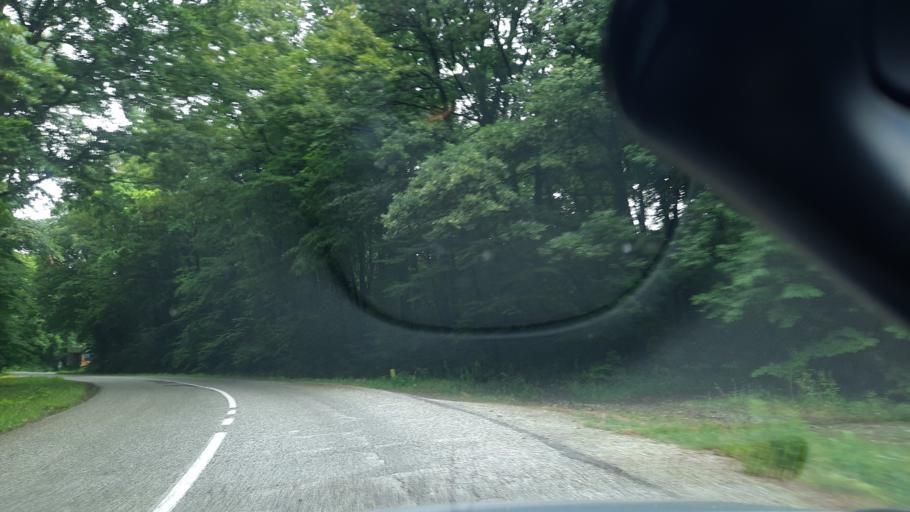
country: RS
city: Glozan
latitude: 45.1438
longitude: 19.5806
